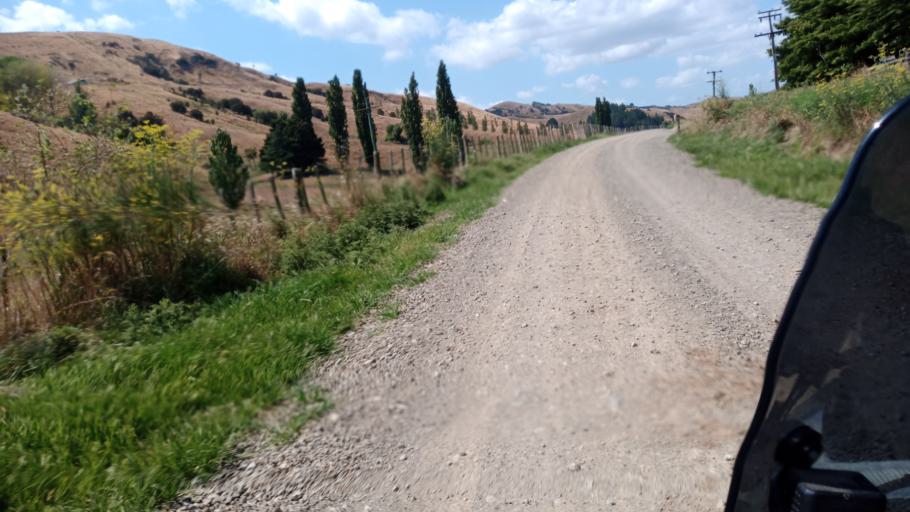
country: NZ
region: Gisborne
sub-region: Gisborne District
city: Gisborne
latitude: -38.4828
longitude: 177.8427
